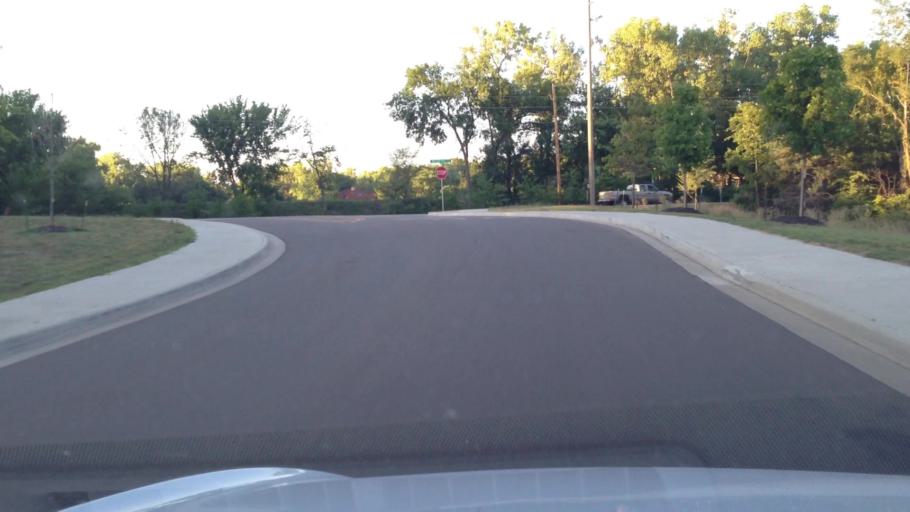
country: US
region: Kansas
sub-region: Douglas County
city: Lawrence
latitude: 38.9563
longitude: -95.2935
